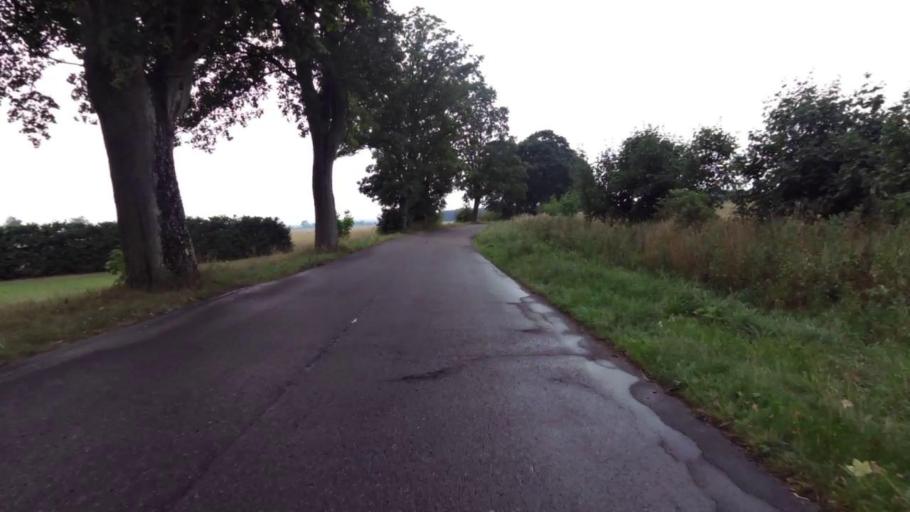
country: PL
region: West Pomeranian Voivodeship
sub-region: Powiat szczecinecki
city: Lubowo
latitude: 53.5892
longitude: 16.3766
